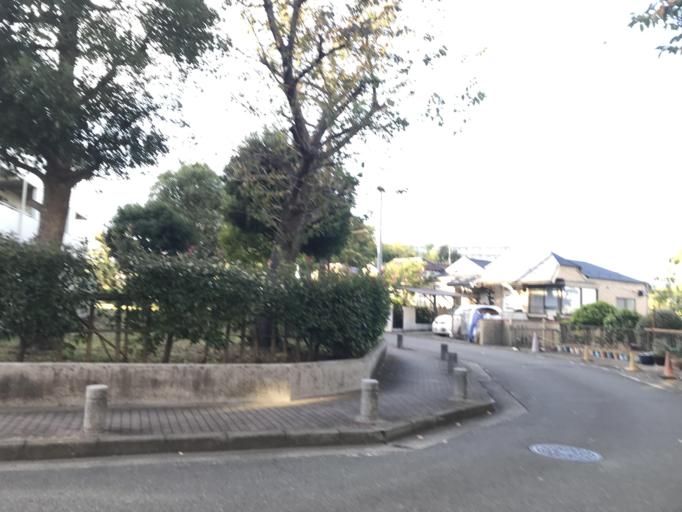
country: JP
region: Kanagawa
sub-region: Kawasaki-shi
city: Kawasaki
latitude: 35.5622
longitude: 139.6304
